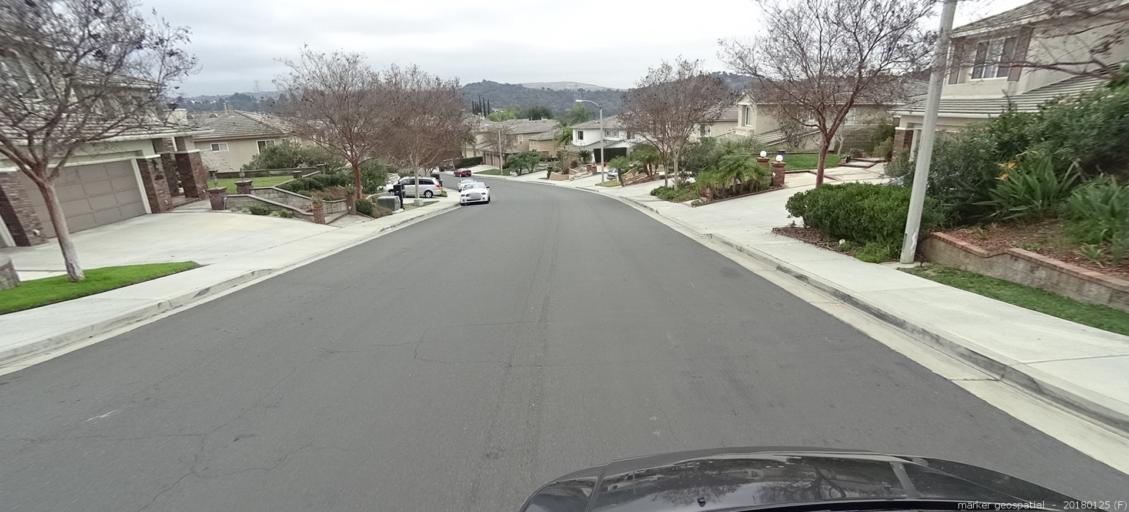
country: US
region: California
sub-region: Los Angeles County
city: Walnut
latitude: 33.9700
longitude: -117.8535
